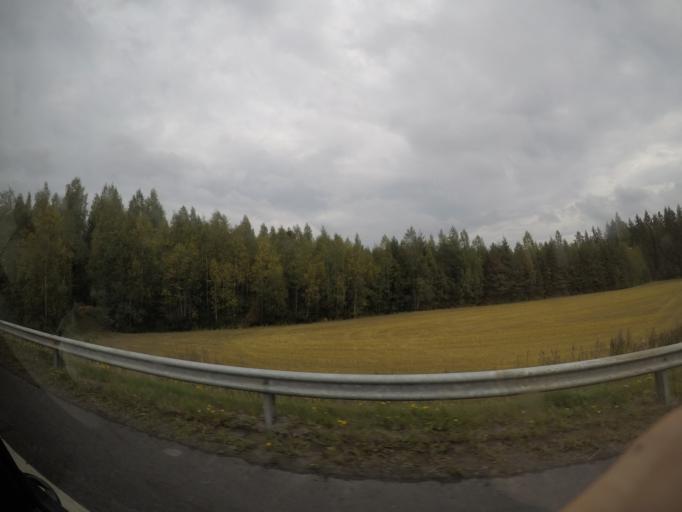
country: FI
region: Haeme
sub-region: Haemeenlinna
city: Parola
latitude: 61.1246
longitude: 24.4182
